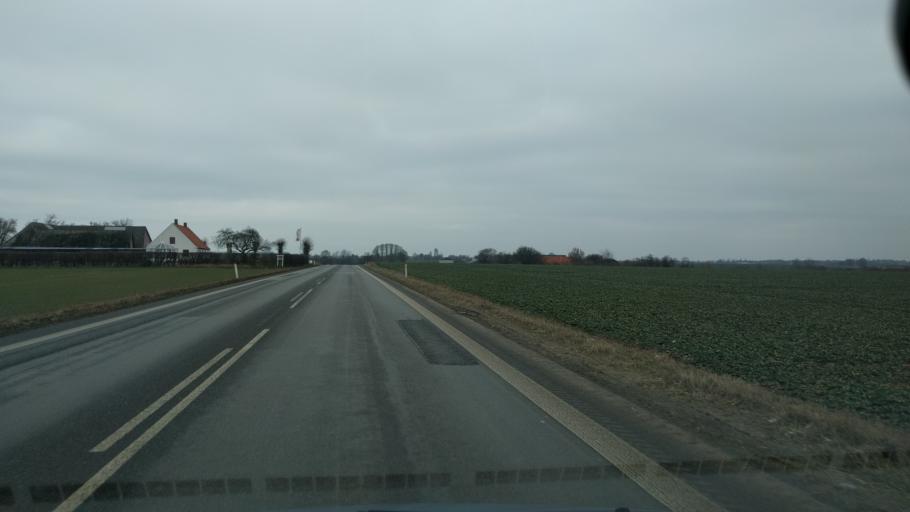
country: DK
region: Zealand
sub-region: Guldborgsund Kommune
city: Stubbekobing
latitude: 54.8729
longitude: 12.0257
